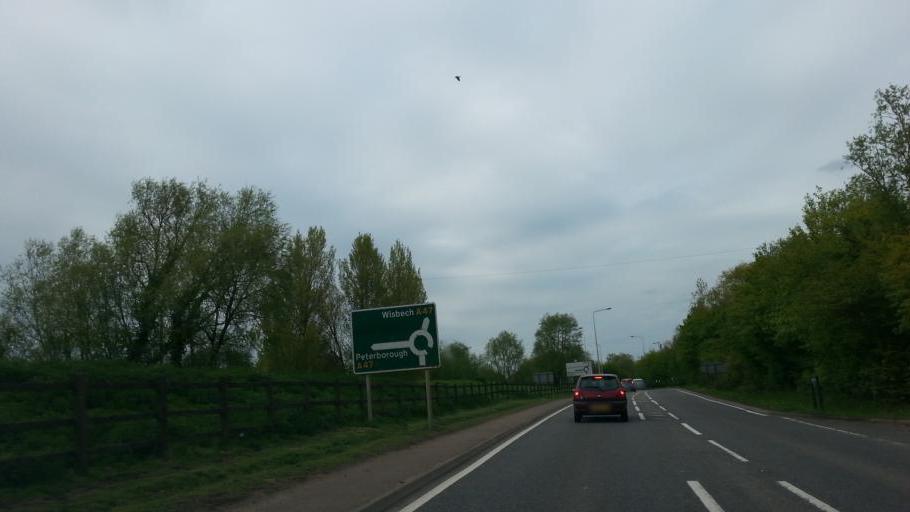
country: GB
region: England
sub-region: Cambridgeshire
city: March
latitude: 52.6050
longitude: 0.0631
